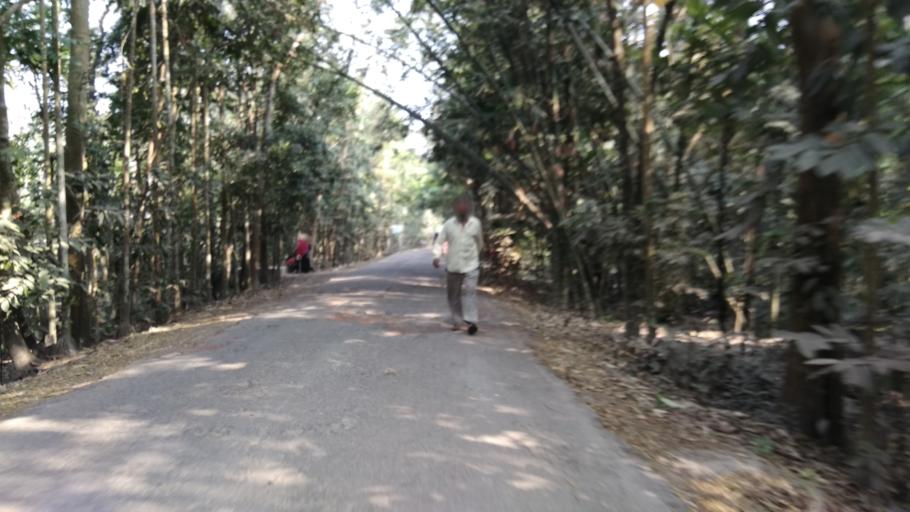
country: BD
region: Barisal
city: Mehendiganj
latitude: 22.9751
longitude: 90.4164
